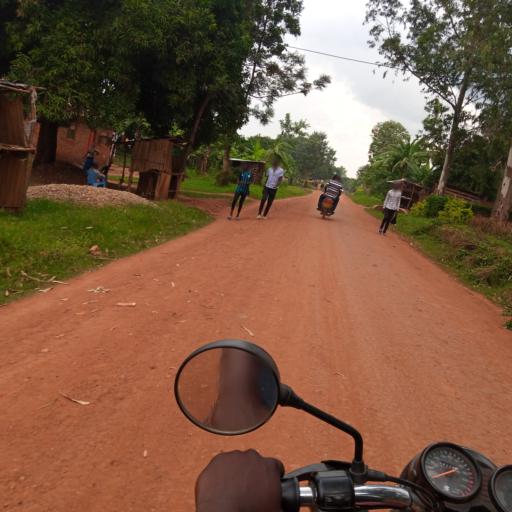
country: UG
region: Eastern Region
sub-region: Mbale District
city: Mbale
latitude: 1.1087
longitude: 34.1809
